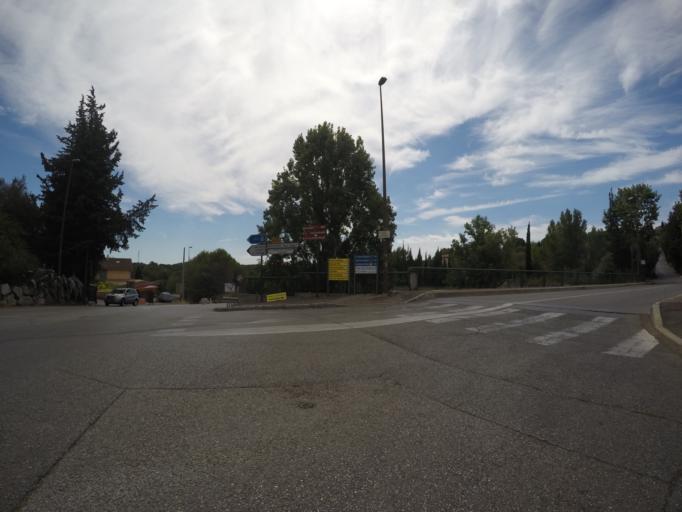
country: FR
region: Provence-Alpes-Cote d'Azur
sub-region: Departement des Alpes-Maritimes
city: Mougins
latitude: 43.6051
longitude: 6.9999
